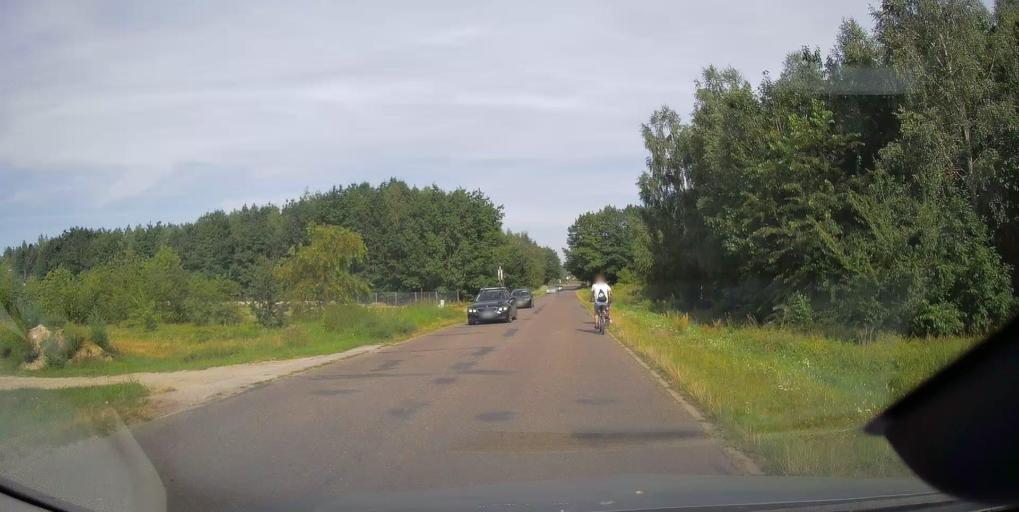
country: PL
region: Lodz Voivodeship
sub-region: Powiat tomaszowski
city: Tomaszow Mazowiecki
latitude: 51.4745
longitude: 19.9939
